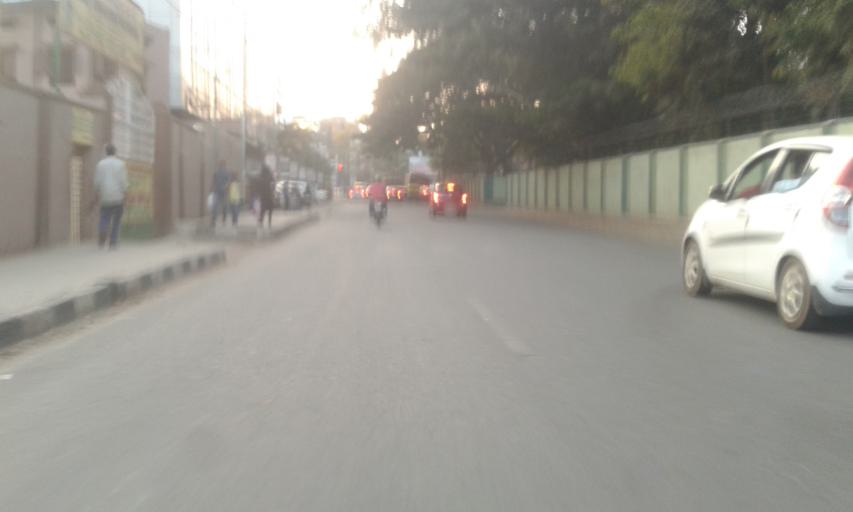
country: IN
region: Karnataka
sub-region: Bangalore Urban
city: Bangalore
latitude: 12.9668
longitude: 77.6125
